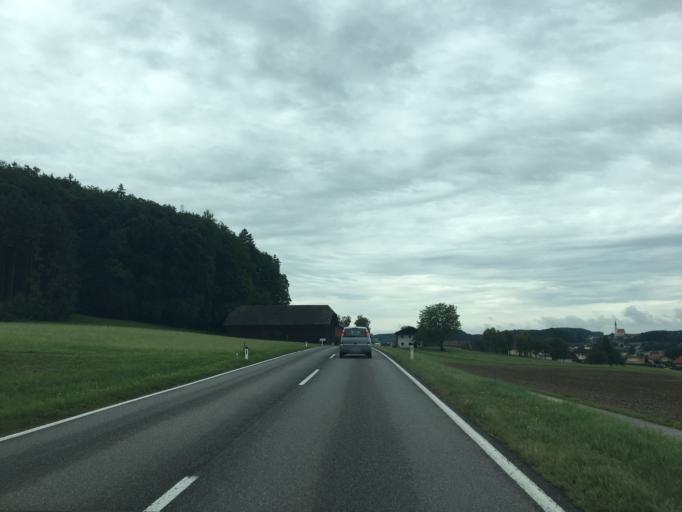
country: AT
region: Salzburg
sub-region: Politischer Bezirk Salzburg-Umgebung
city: Dorfbeuern
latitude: 48.0527
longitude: 12.9847
